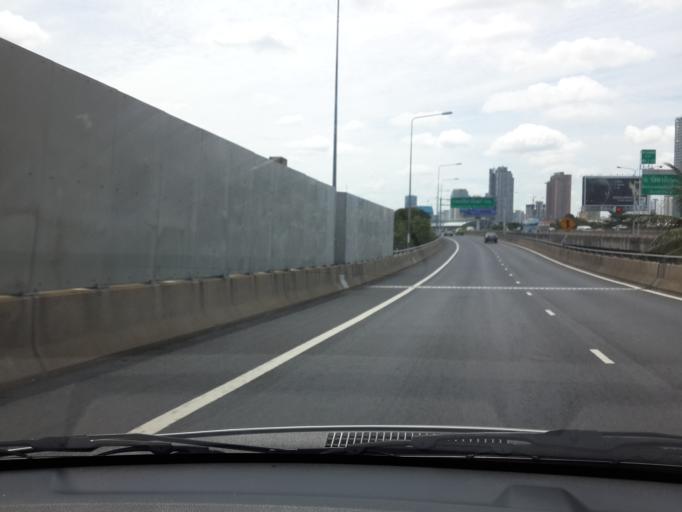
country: TH
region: Bangkok
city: Din Daeng
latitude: 13.7567
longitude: 100.5509
